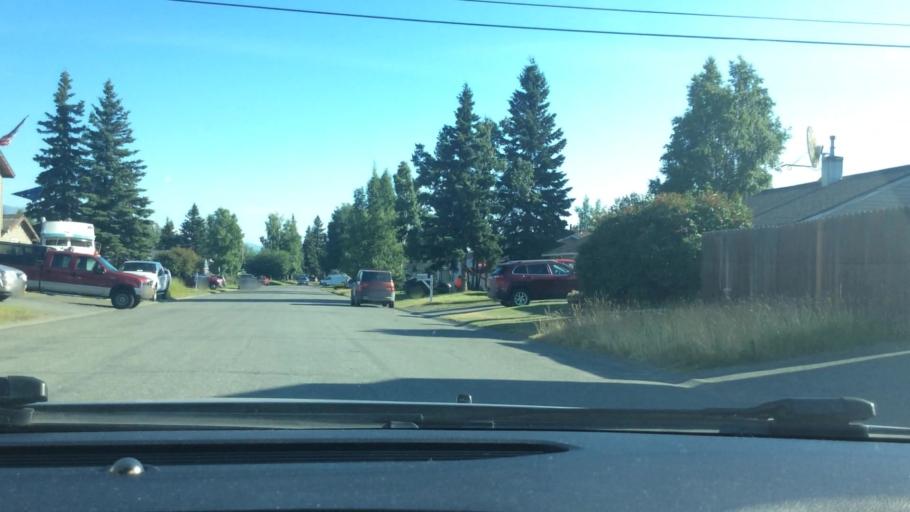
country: US
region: Alaska
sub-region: Anchorage Municipality
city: Anchorage
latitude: 61.2088
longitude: -149.7701
